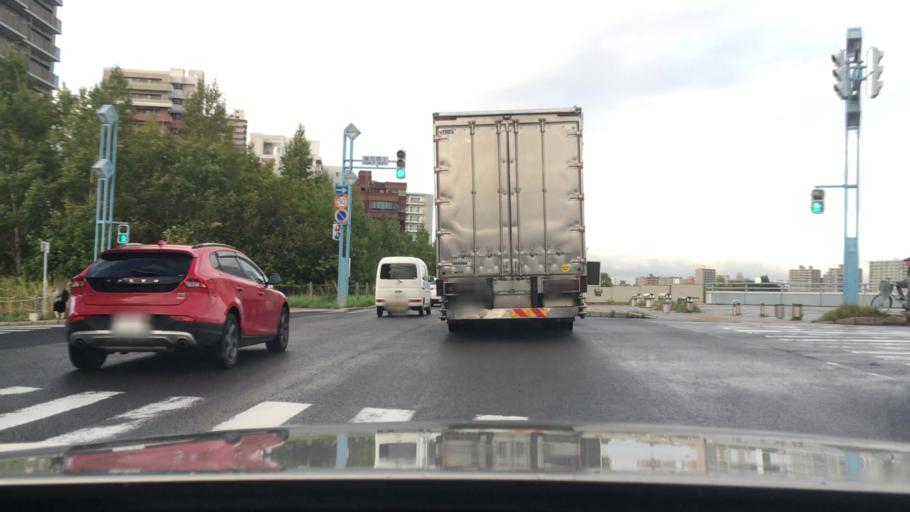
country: JP
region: Hokkaido
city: Sapporo
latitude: 43.0397
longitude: 141.3568
